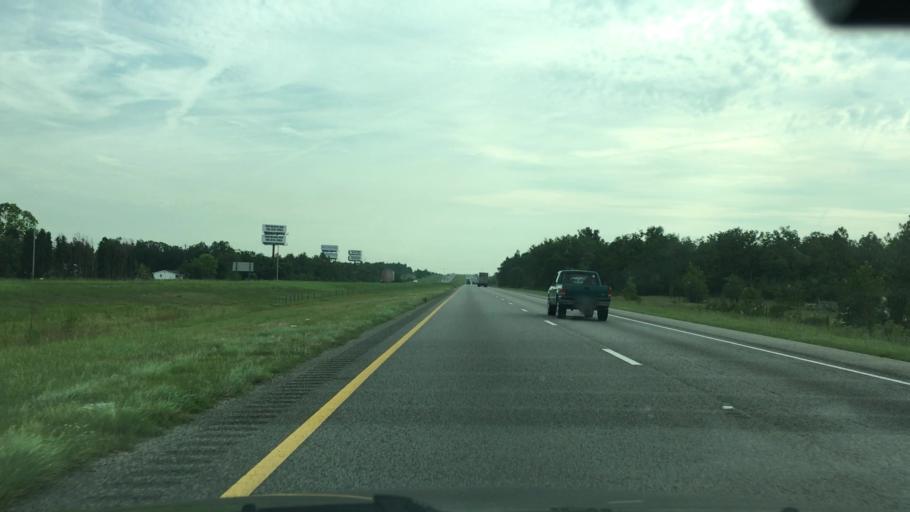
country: US
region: South Carolina
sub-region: Lexington County
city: Batesburg
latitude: 33.7121
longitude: -81.5811
